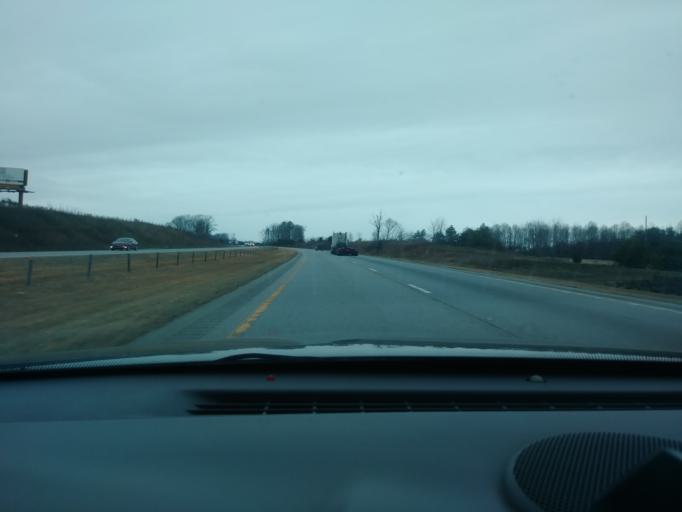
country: US
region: North Carolina
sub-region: Yadkin County
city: Jonesville
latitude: 36.1400
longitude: -80.8687
